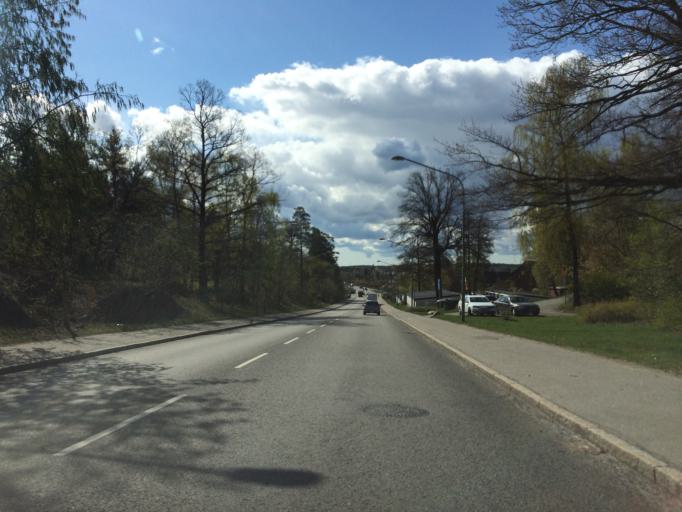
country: SE
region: Stockholm
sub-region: Huddinge Kommun
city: Segeltorp
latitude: 59.2930
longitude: 17.9462
